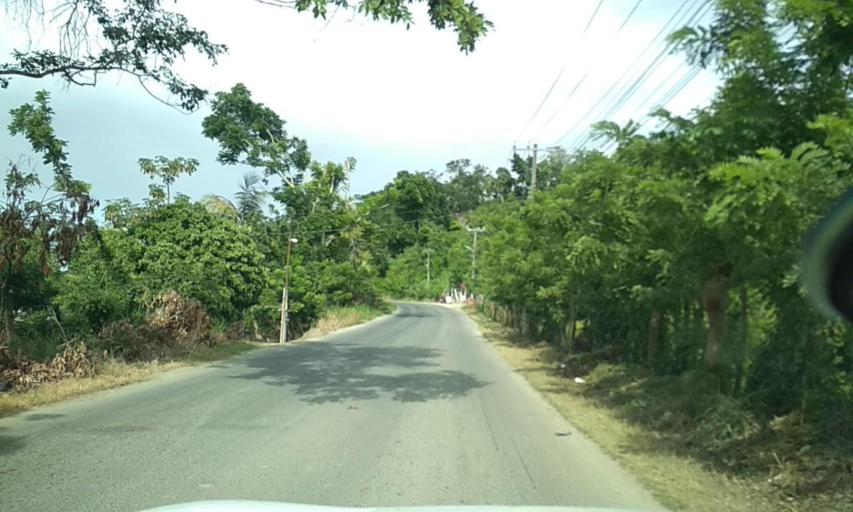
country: MX
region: Veracruz
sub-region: Papantla
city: Residencial Tajin
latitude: 20.6423
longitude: -97.3616
